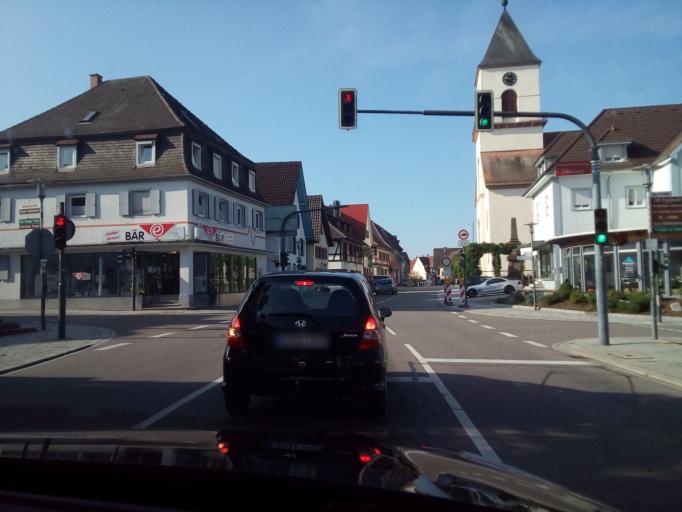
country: DE
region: Baden-Wuerttemberg
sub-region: Freiburg Region
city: Renchen
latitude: 48.5883
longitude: 8.0138
